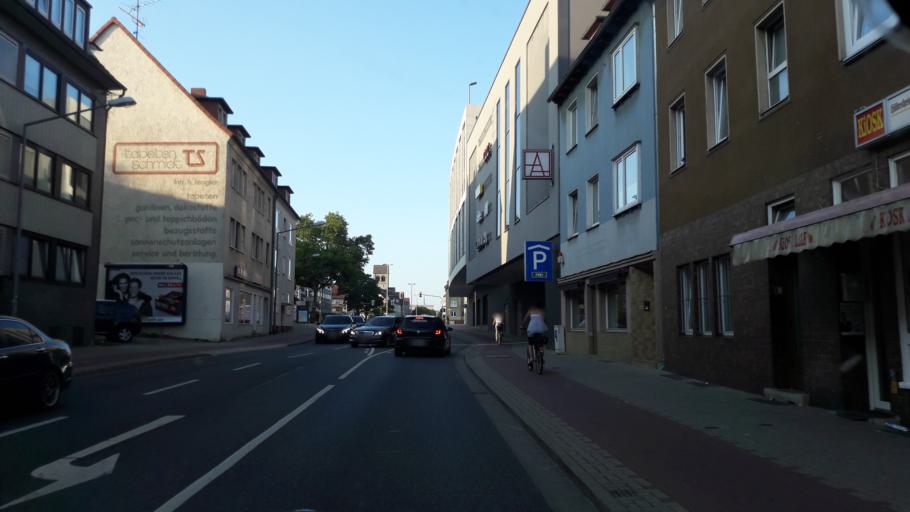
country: DE
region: Lower Saxony
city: Hildesheim
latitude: 52.1535
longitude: 9.9484
